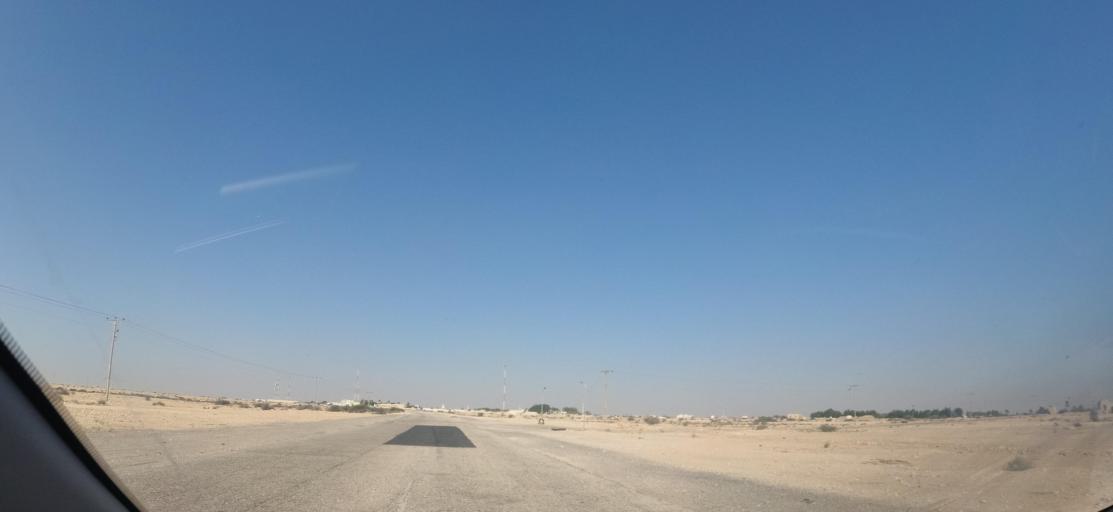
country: QA
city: Al Jumayliyah
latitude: 25.6099
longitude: 51.0778
